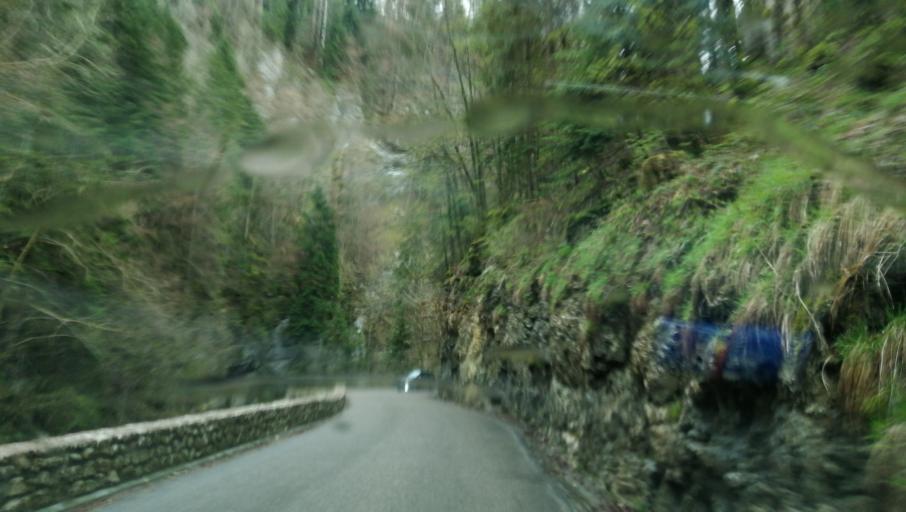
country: FR
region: Rhone-Alpes
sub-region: Departement de l'Isere
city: Villard-de-Lans
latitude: 45.0770
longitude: 5.5212
